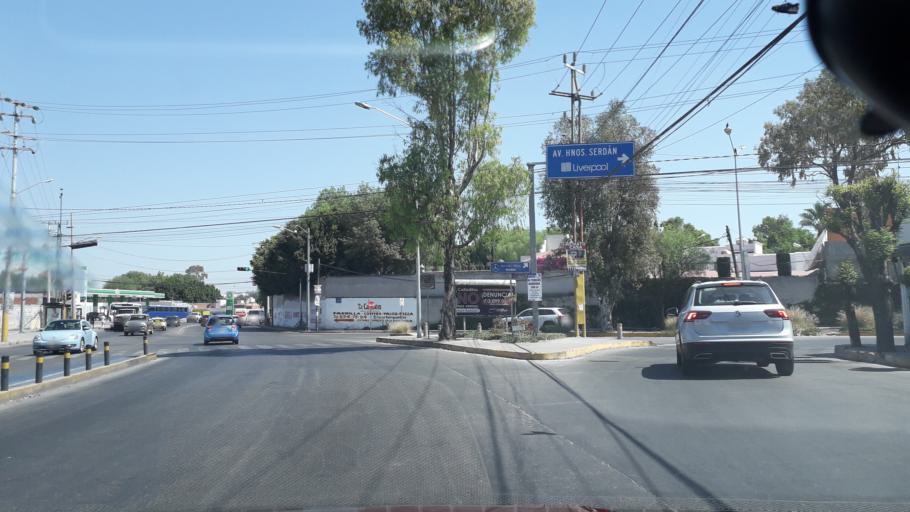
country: MX
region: Puebla
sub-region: Cuautlancingo
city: Sanctorum
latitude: 19.0874
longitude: -98.2379
